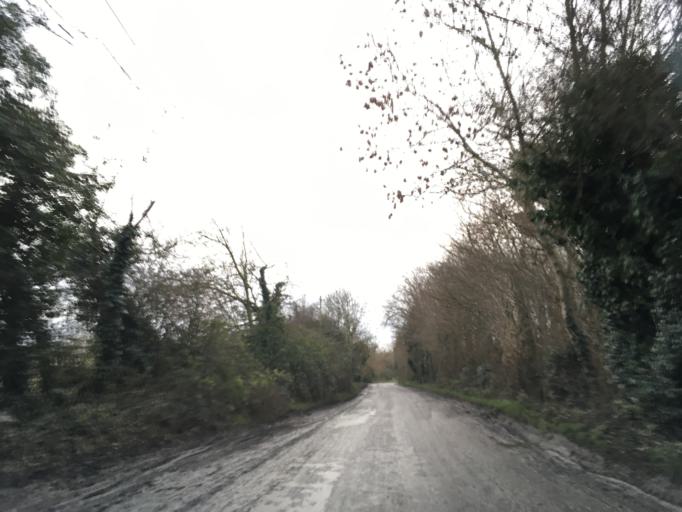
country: GB
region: England
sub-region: South Gloucestershire
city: Tytherington
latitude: 51.5802
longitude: -2.4914
